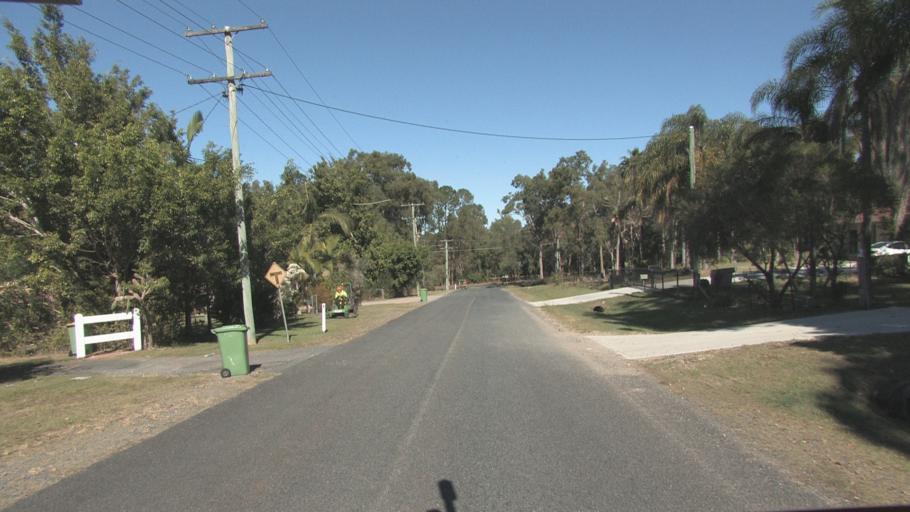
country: AU
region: Queensland
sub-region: Logan
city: Park Ridge South
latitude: -27.7153
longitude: 153.0405
